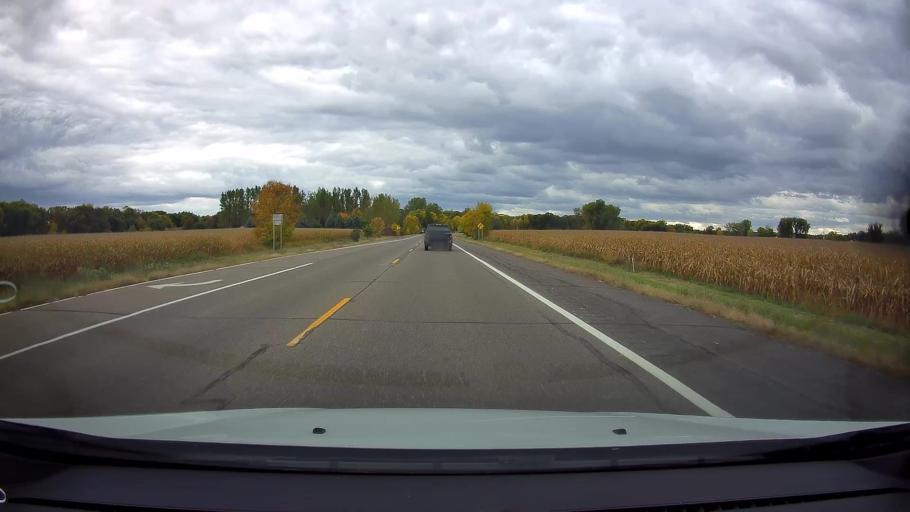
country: US
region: Minnesota
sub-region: Chisago County
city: Chisago City
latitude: 45.3475
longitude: -92.9118
